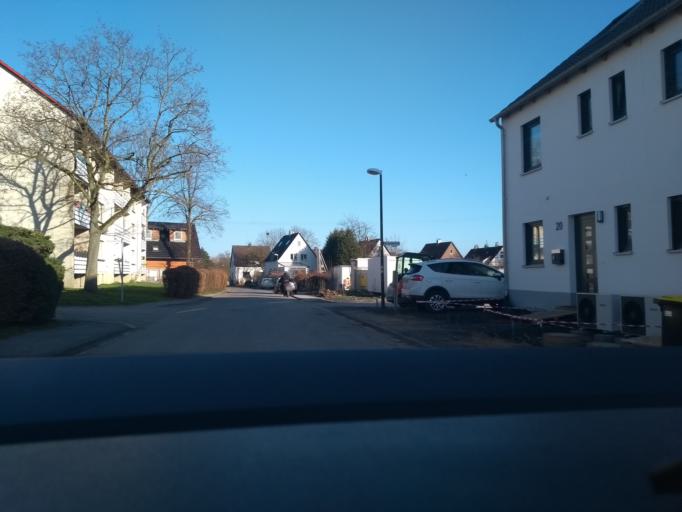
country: DE
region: North Rhine-Westphalia
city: Waltrop
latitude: 51.5945
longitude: 7.4601
